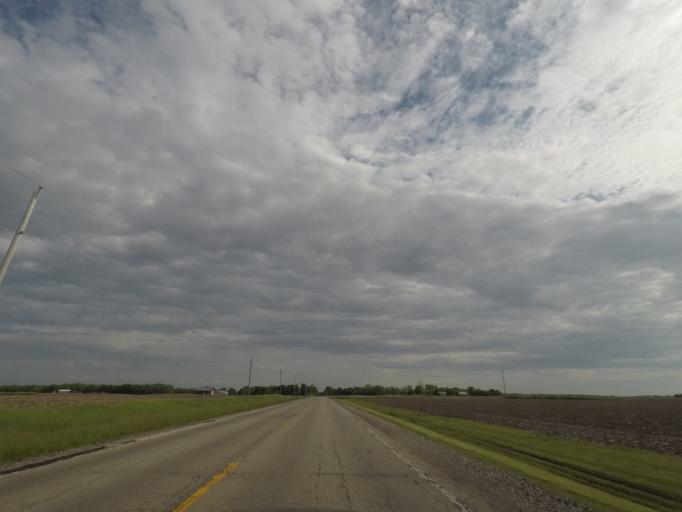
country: US
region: Illinois
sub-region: Logan County
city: Mount Pulaski
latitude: 40.0401
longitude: -89.2815
